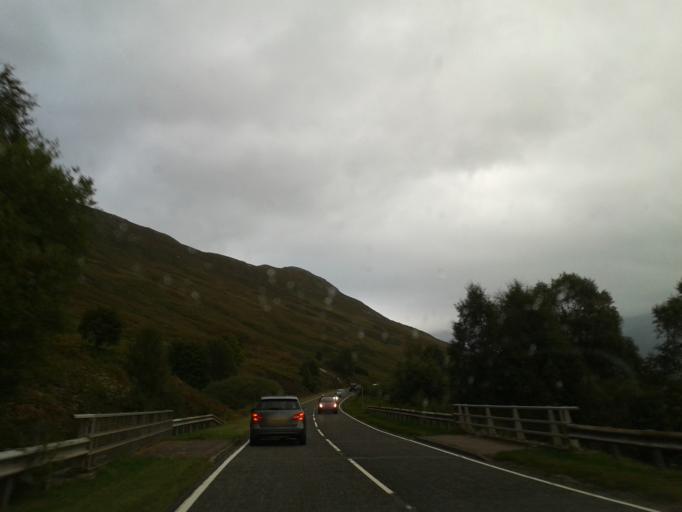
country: GB
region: Scotland
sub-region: Highland
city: Spean Bridge
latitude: 57.1535
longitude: -5.1314
